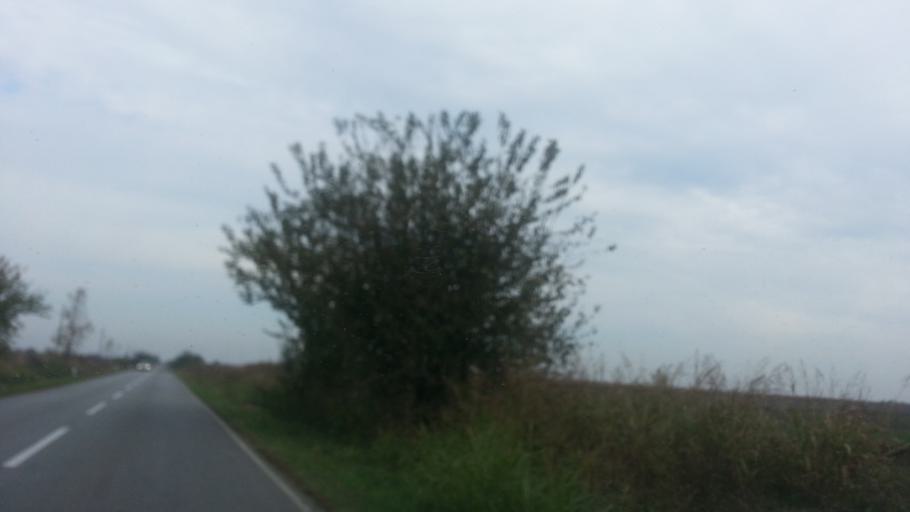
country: RS
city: Surduk
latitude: 45.0532
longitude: 20.3316
